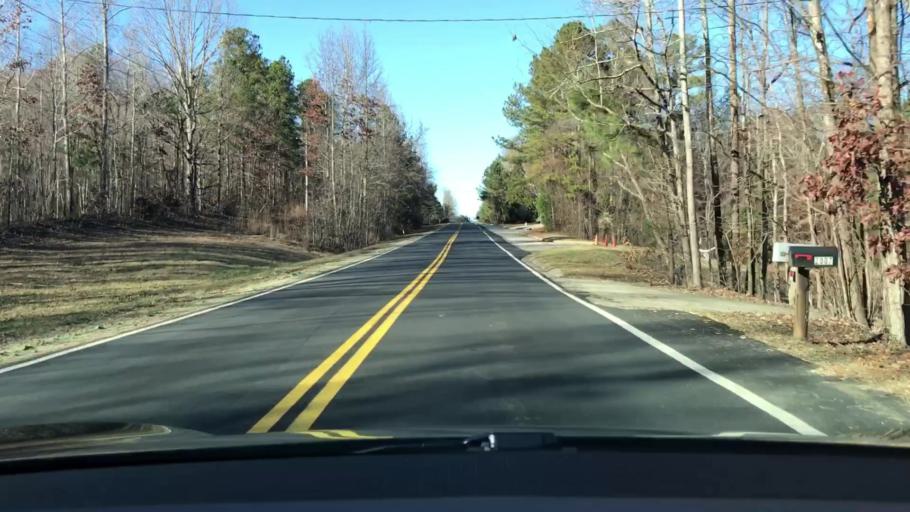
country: US
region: Georgia
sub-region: Barrow County
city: Auburn
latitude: 34.0852
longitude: -83.8684
